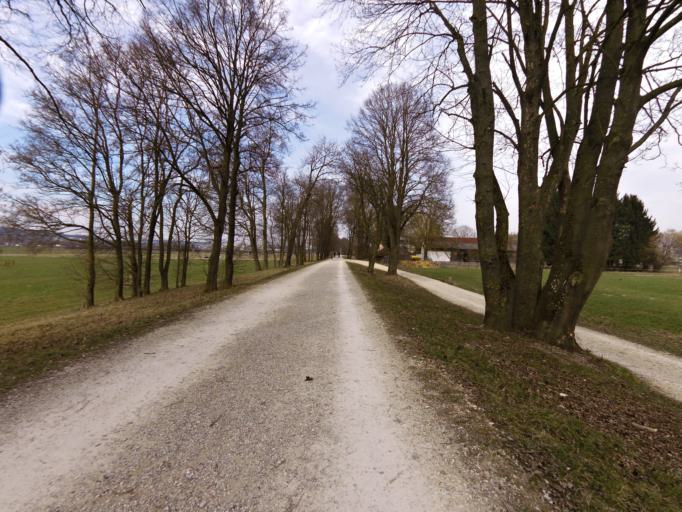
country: DE
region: Bavaria
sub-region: Lower Bavaria
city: Tiefenbach
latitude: 48.5343
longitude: 12.1120
